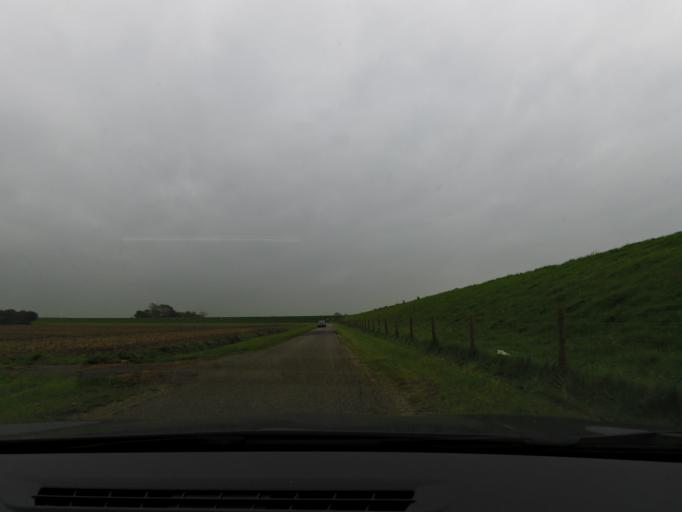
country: NL
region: South Holland
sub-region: Gemeente Goeree-Overflakkee
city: Middelharnis
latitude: 51.7976
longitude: 4.2400
